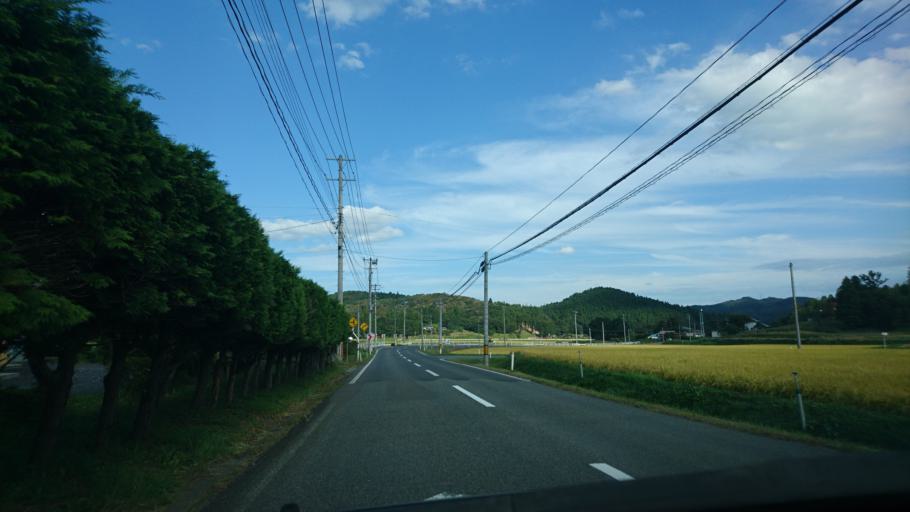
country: JP
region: Iwate
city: Ichinoseki
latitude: 38.8368
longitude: 141.2364
